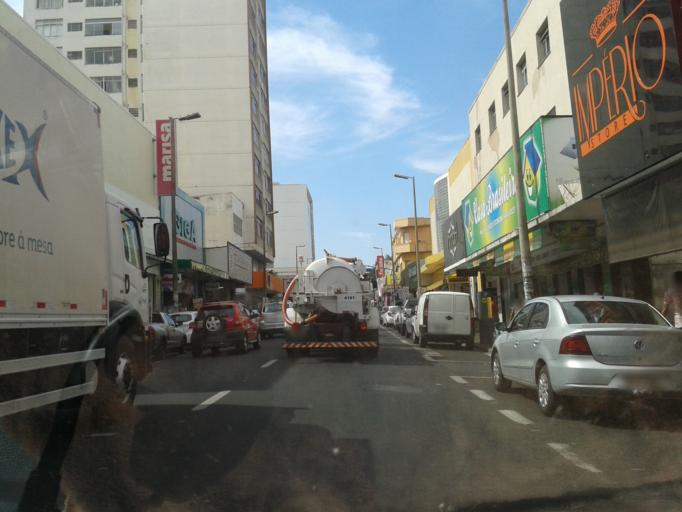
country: BR
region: Minas Gerais
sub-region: Uberlandia
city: Uberlandia
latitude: -18.9183
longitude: -48.2778
